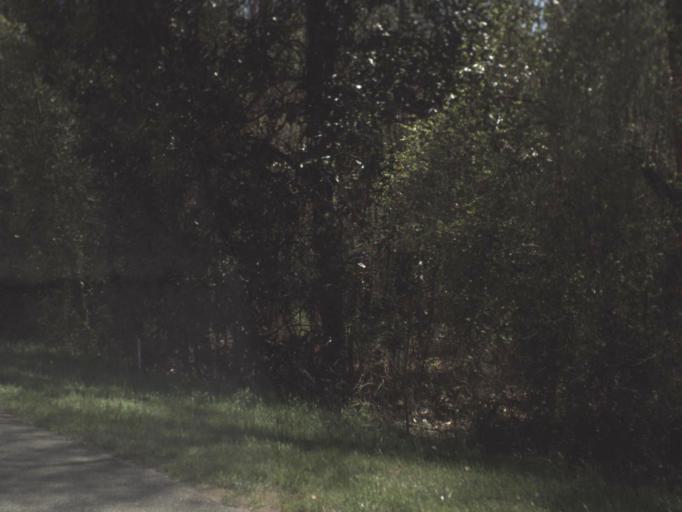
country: US
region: Florida
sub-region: Calhoun County
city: Blountstown
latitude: 30.4345
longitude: -85.1769
